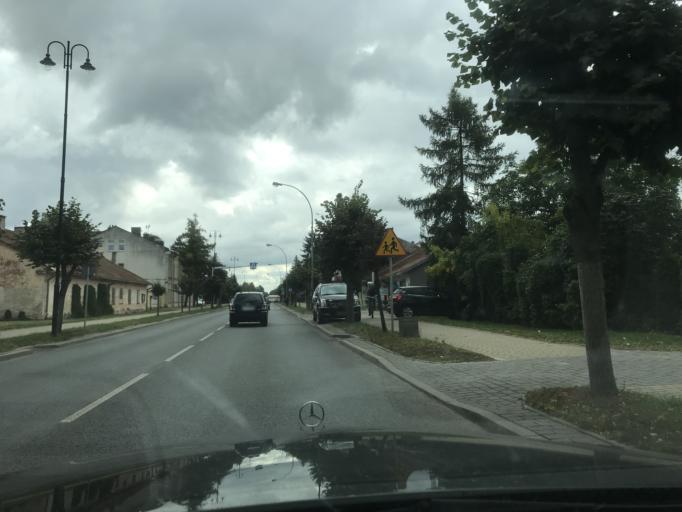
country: PL
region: Lublin Voivodeship
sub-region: Powiat janowski
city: Janow Lubelski
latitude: 50.7032
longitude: 22.4168
